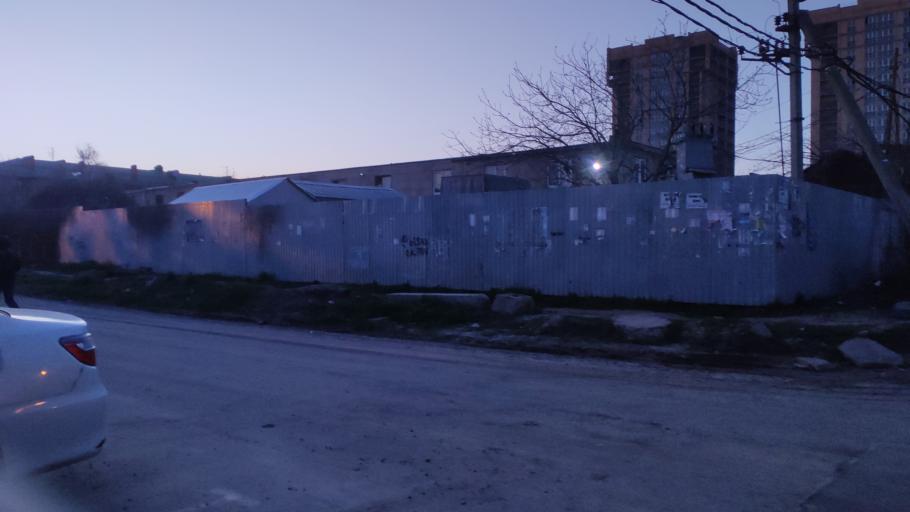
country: RU
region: Krasnodarskiy
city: Krasnodar
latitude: 45.0817
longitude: 39.0117
